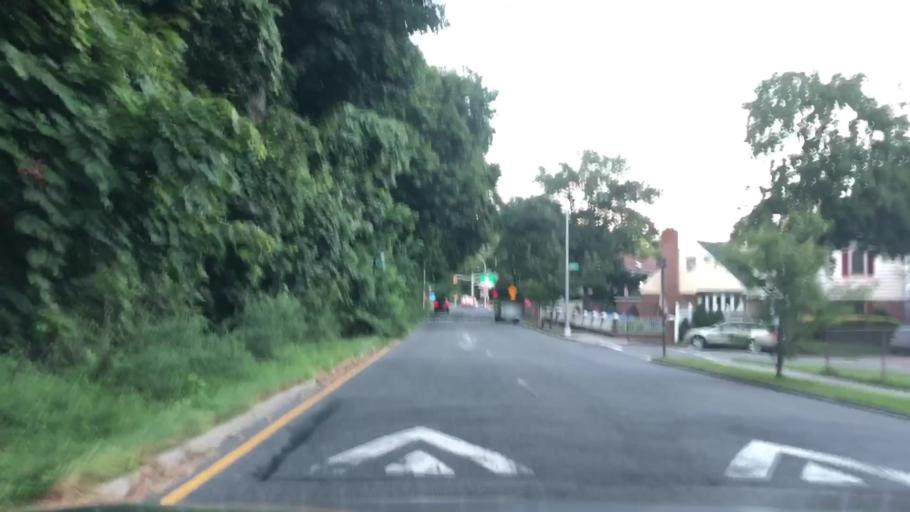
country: US
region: New York
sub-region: Nassau County
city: Bellerose Terrace
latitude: 40.7359
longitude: -73.7414
